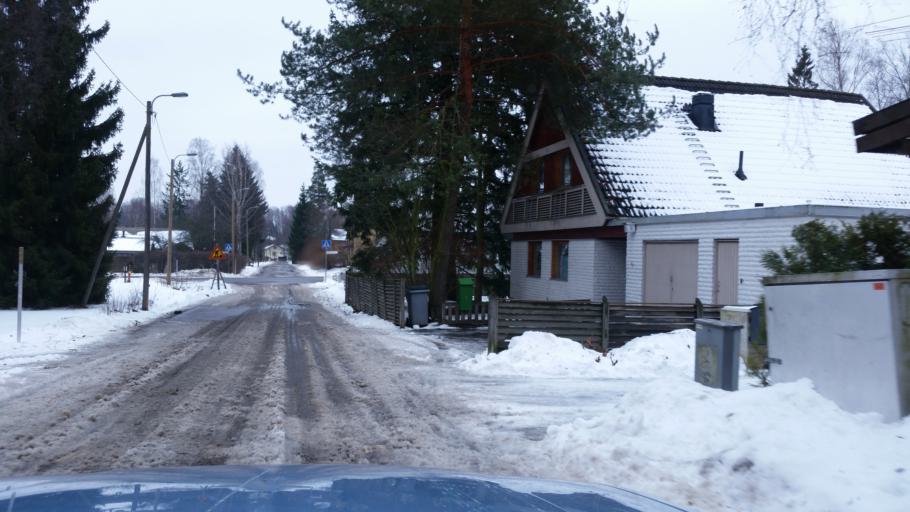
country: FI
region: Uusimaa
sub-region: Helsinki
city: Vantaa
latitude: 60.2488
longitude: 25.0856
